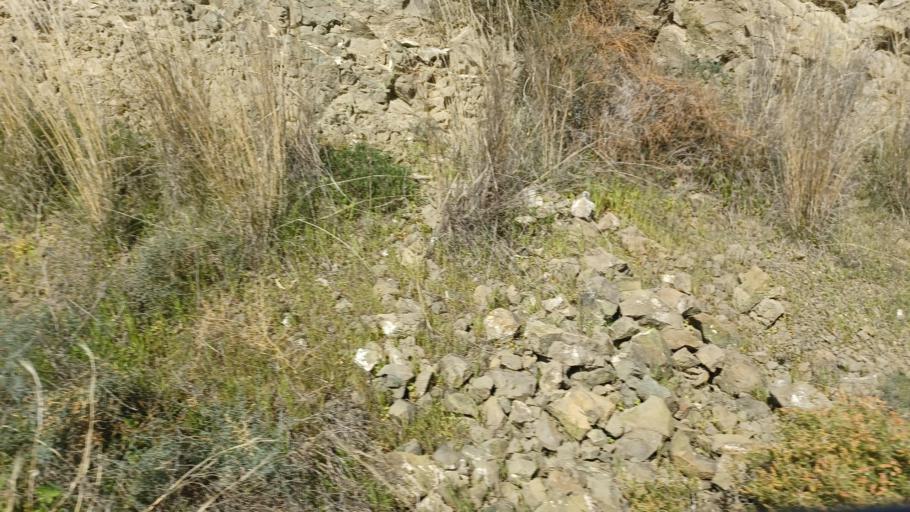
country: CY
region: Lefkosia
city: Lefka
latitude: 35.0998
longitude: 32.8860
